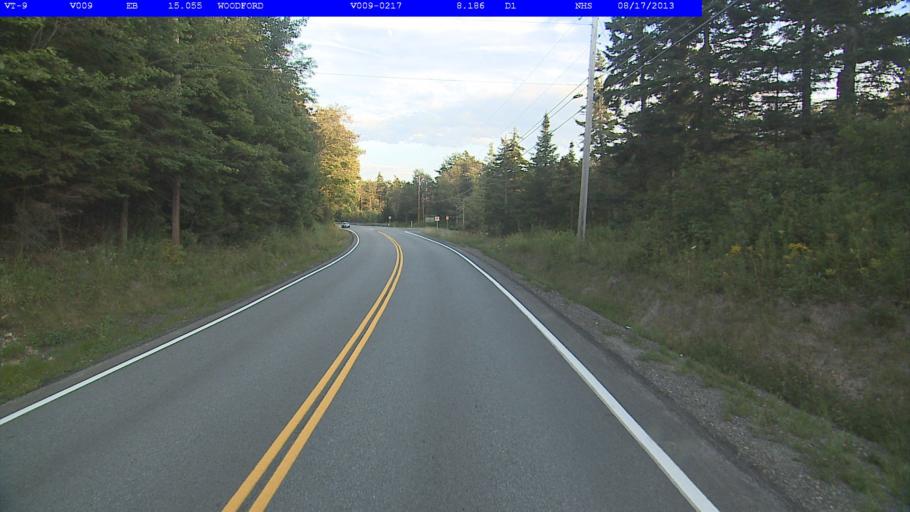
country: US
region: Vermont
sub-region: Bennington County
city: Bennington
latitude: 42.8930
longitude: -73.0362
